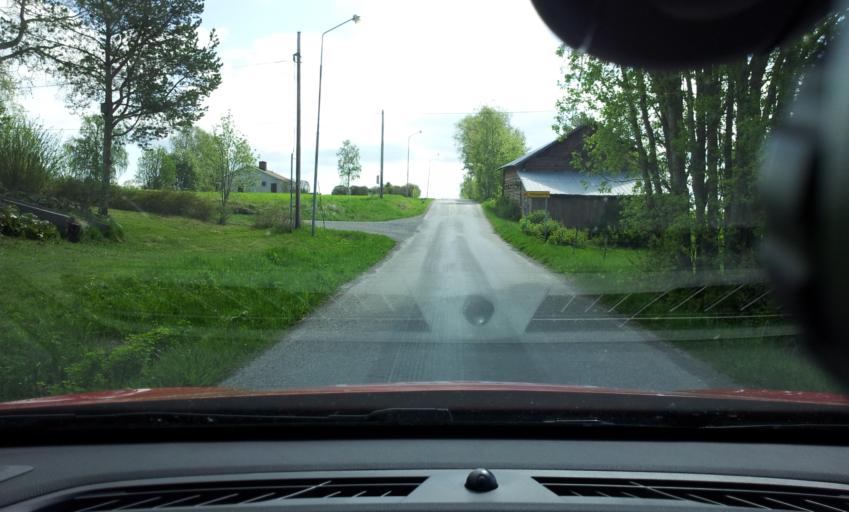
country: SE
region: Jaemtland
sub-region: OEstersunds Kommun
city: Ostersund
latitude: 63.0137
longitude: 14.5992
